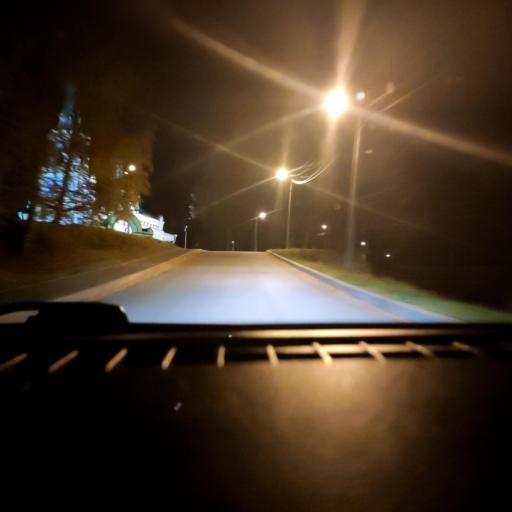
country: RU
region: Perm
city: Perm
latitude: 58.0140
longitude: 56.2675
